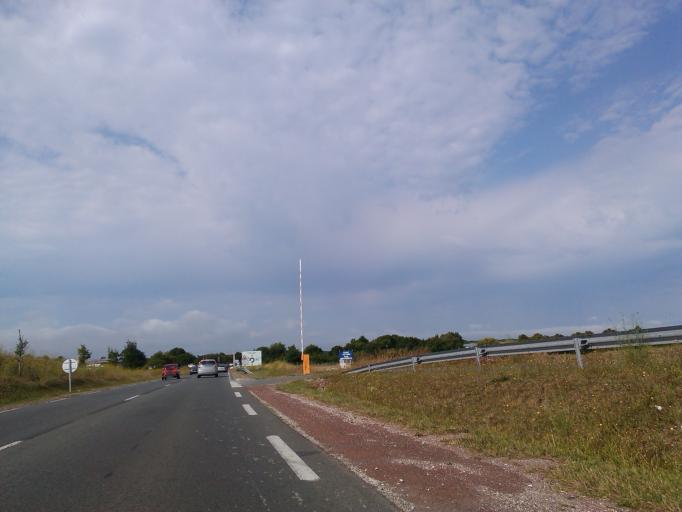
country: FR
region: Poitou-Charentes
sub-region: Departement de la Charente-Maritime
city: La Tremblade
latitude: 45.7580
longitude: -1.1359
